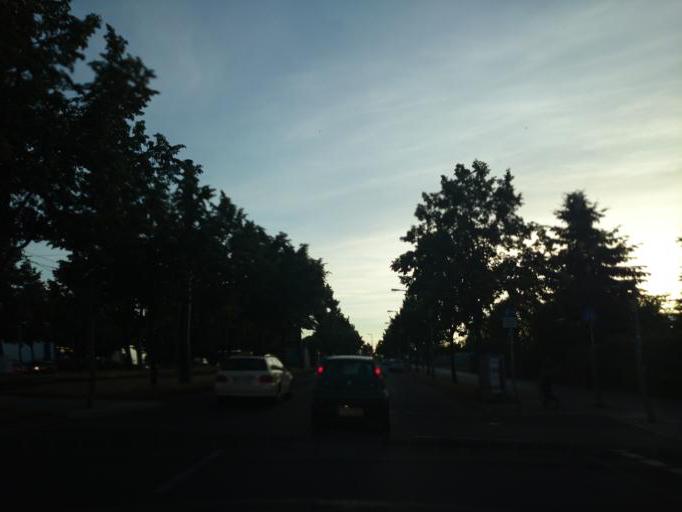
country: DE
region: Berlin
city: Gesundbrunnen
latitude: 52.5546
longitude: 13.4025
